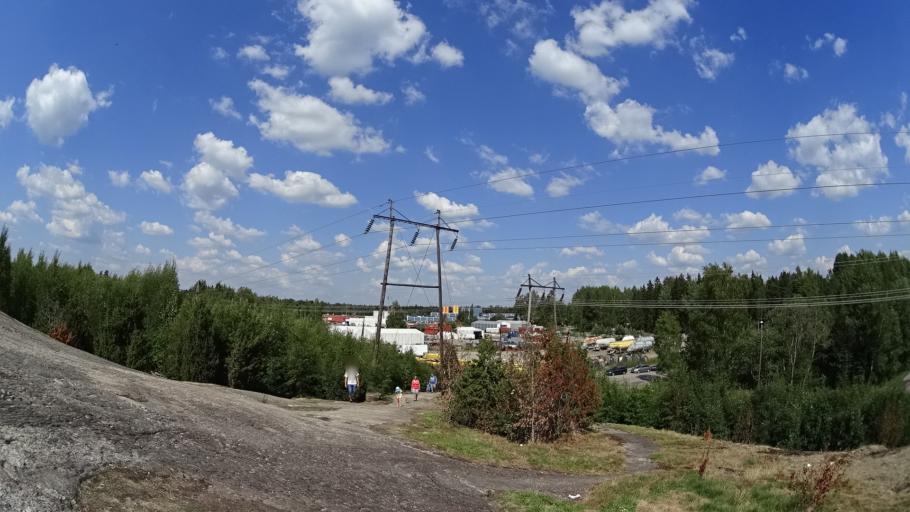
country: FI
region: Uusimaa
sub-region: Helsinki
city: Vantaa
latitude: 60.3396
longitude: 24.9948
